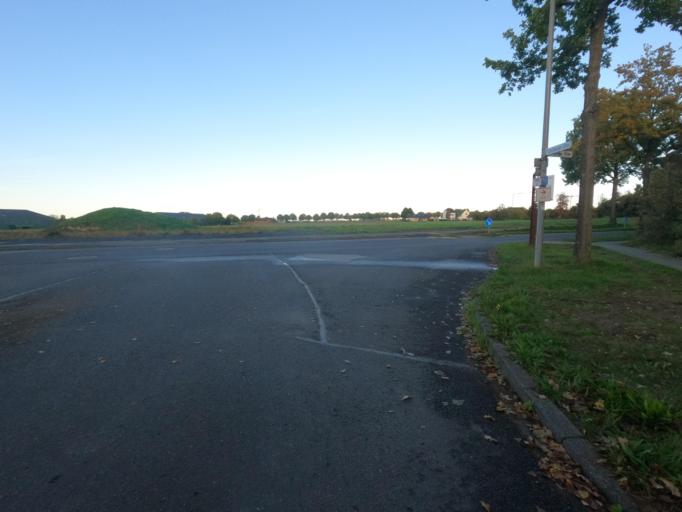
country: DE
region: North Rhine-Westphalia
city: Erkelenz
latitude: 51.0614
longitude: 6.3060
